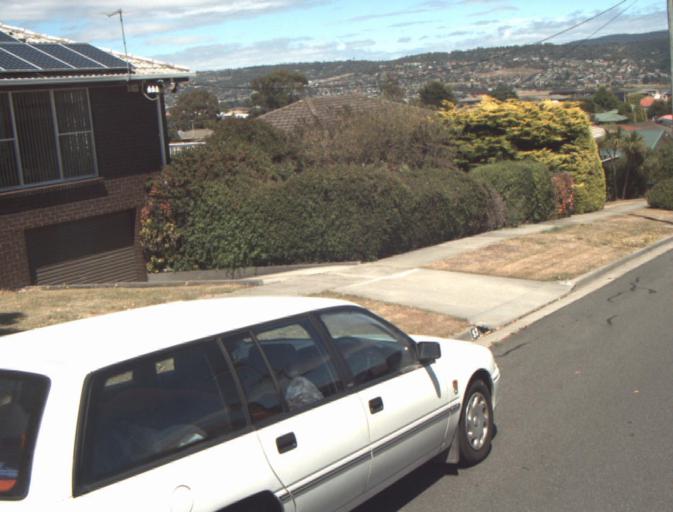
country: AU
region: Tasmania
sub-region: Launceston
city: Mayfield
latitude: -41.3842
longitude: 147.1176
